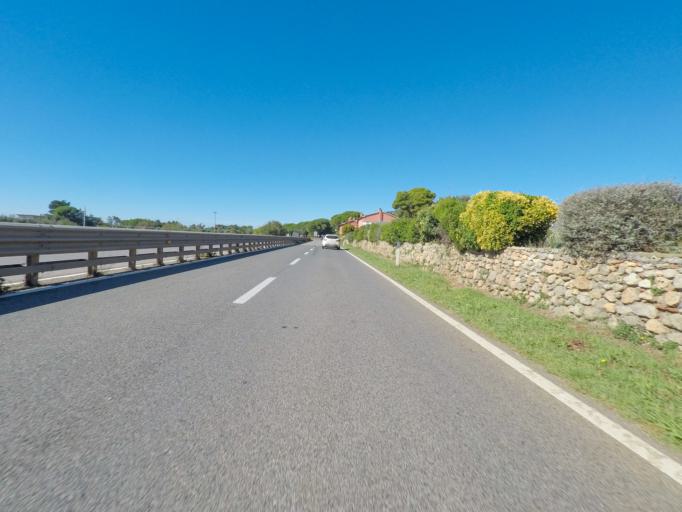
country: IT
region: Tuscany
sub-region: Provincia di Grosseto
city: Orbetello Scalo
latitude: 42.4350
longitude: 11.2808
